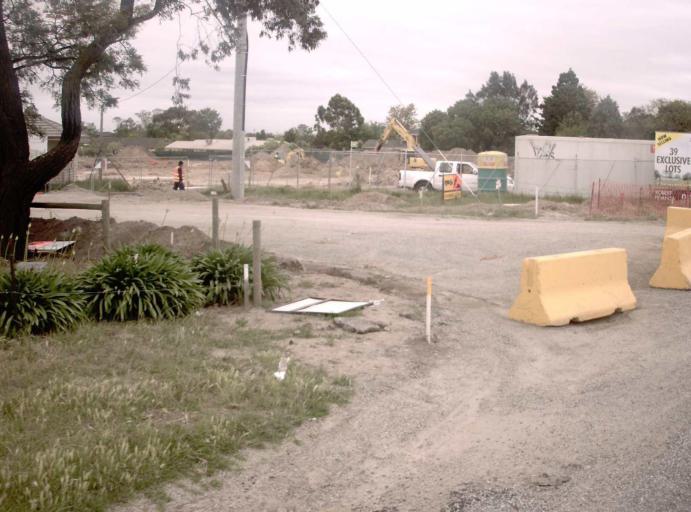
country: AU
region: Victoria
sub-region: Casey
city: Lynbrook
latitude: -38.0450
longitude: 145.2652
